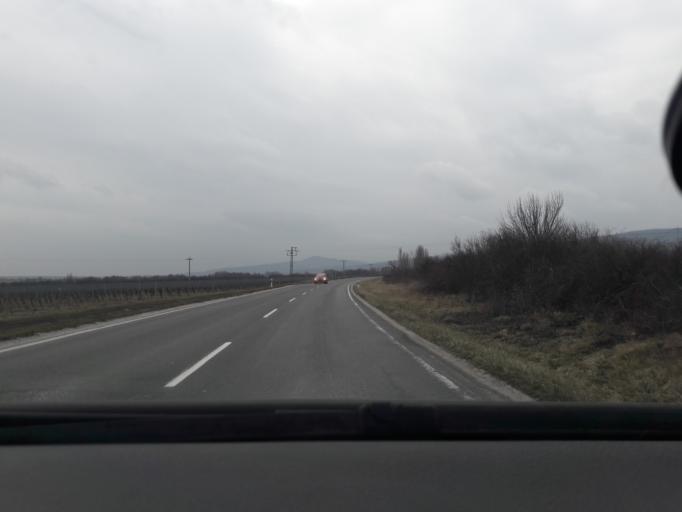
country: SK
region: Trnavsky
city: Smolenice
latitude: 48.4248
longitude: 17.4119
